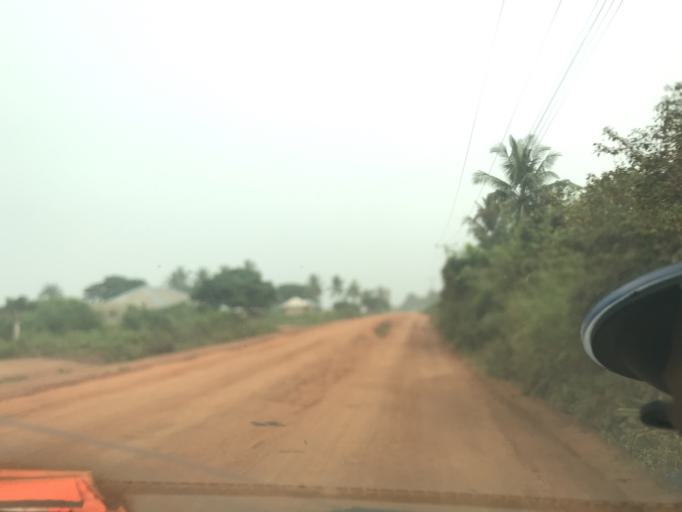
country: NG
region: Ogun
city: Ado Odo
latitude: 6.5418
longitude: 2.9494
